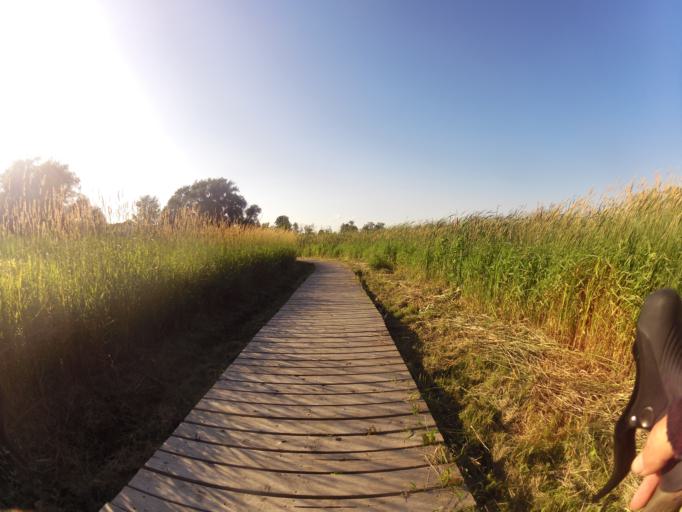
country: CA
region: Ontario
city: Bells Corners
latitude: 45.2743
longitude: -75.7024
